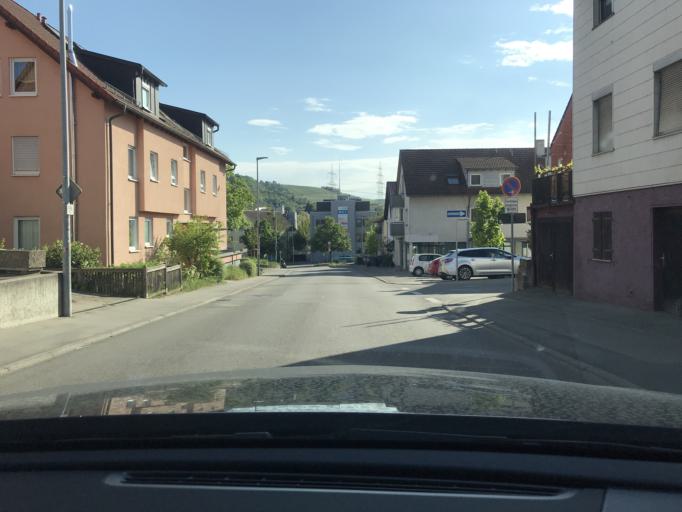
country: DE
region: Baden-Wuerttemberg
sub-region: Regierungsbezirk Stuttgart
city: Weinstadt-Endersbach
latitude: 48.8079
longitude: 9.3864
